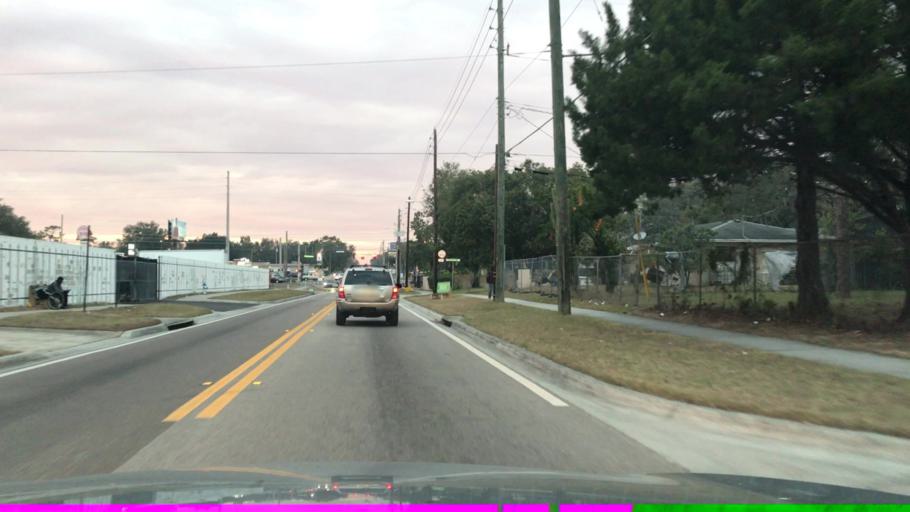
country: US
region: Florida
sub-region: Orange County
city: Pine Hills
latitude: 28.5758
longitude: -81.4677
